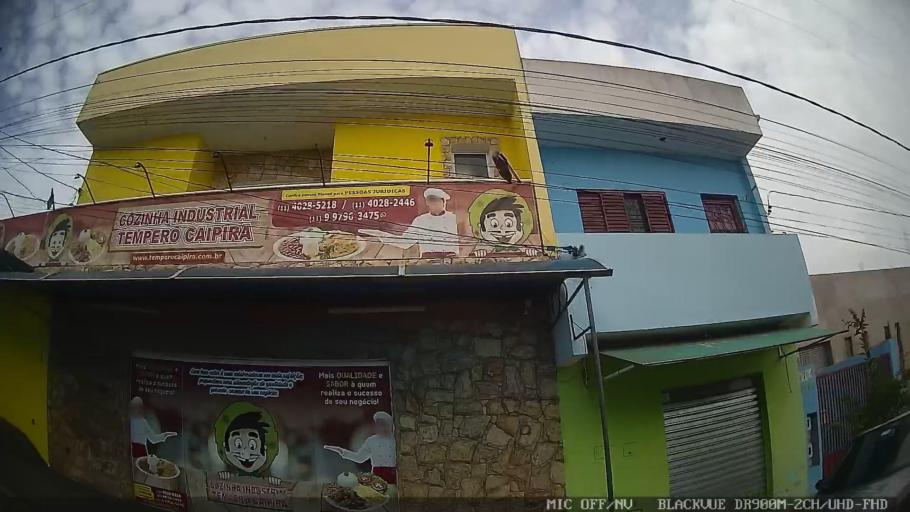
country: BR
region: Sao Paulo
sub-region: Salto
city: Salto
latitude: -23.2215
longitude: -47.2701
